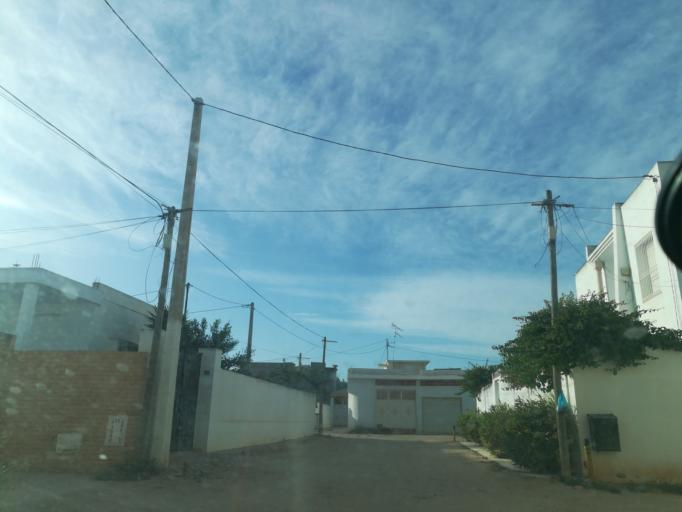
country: TN
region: Safaqis
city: Al Qarmadah
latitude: 34.8101
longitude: 10.7607
